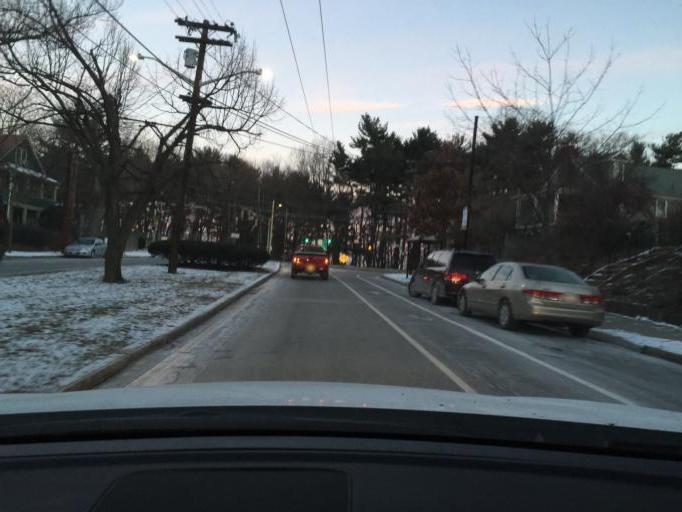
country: US
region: Massachusetts
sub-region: Middlesex County
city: Belmont
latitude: 42.3781
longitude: -71.1470
